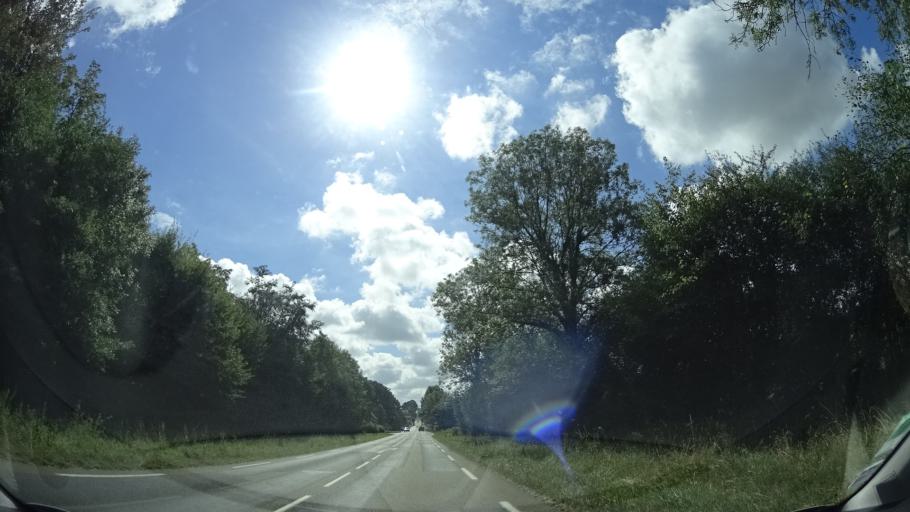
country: FR
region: Pays de la Loire
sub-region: Departement de la Mayenne
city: Bonchamp-les-Laval
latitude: 48.0363
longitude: -0.7099
